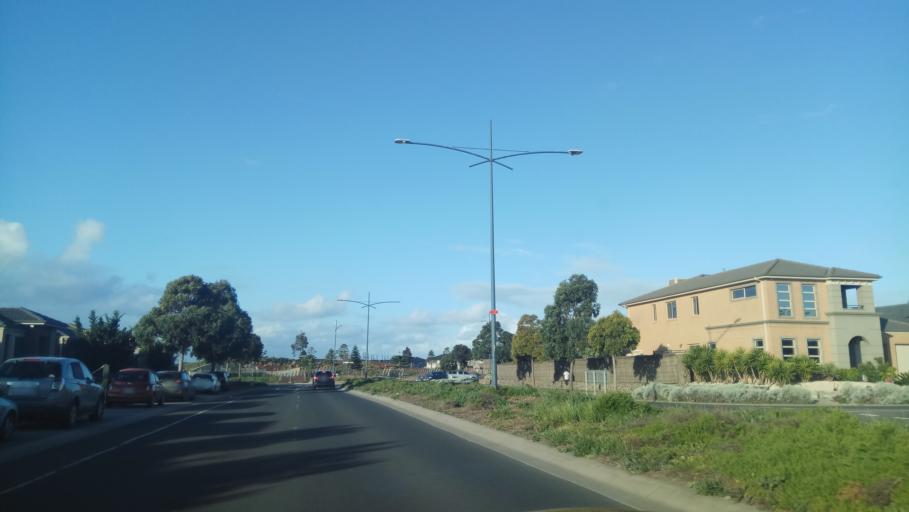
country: AU
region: Victoria
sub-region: Wyndham
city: Point Cook
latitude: -37.9101
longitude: 144.7739
